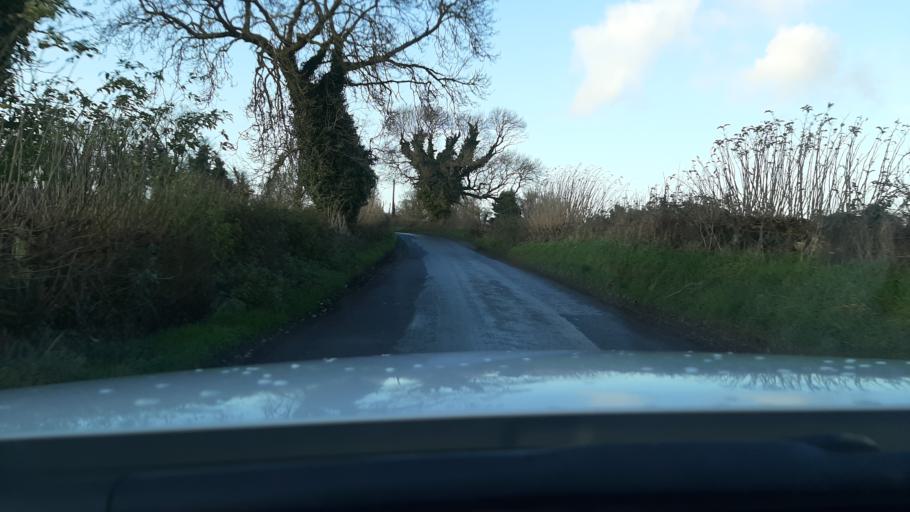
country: IE
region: Leinster
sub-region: Kildare
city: Kildare
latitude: 53.1672
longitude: -6.9234
